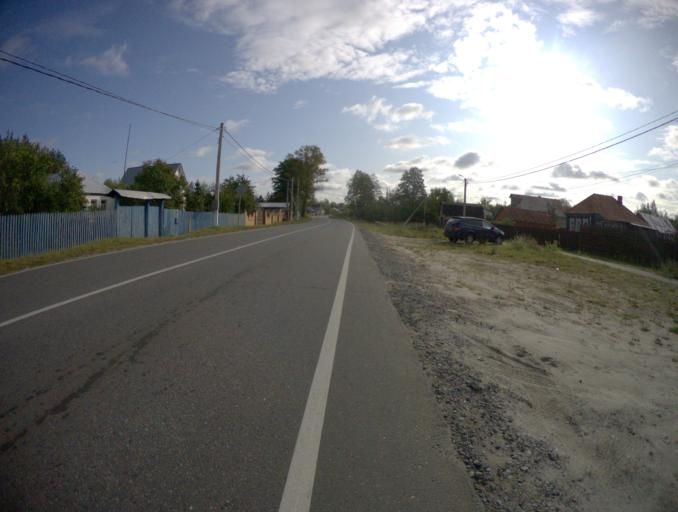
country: RU
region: Moskovskaya
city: Roshal'
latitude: 55.6574
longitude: 39.8154
